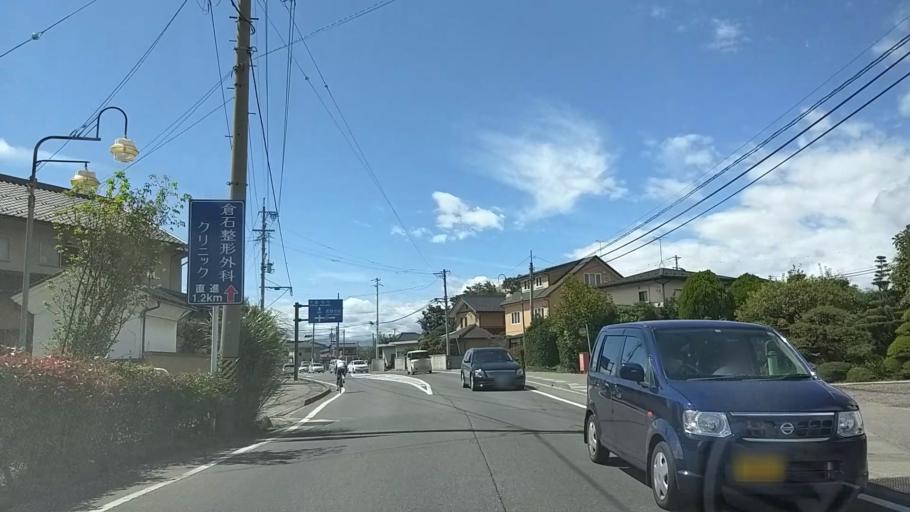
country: JP
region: Nagano
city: Suzaka
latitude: 36.6199
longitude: 138.2544
